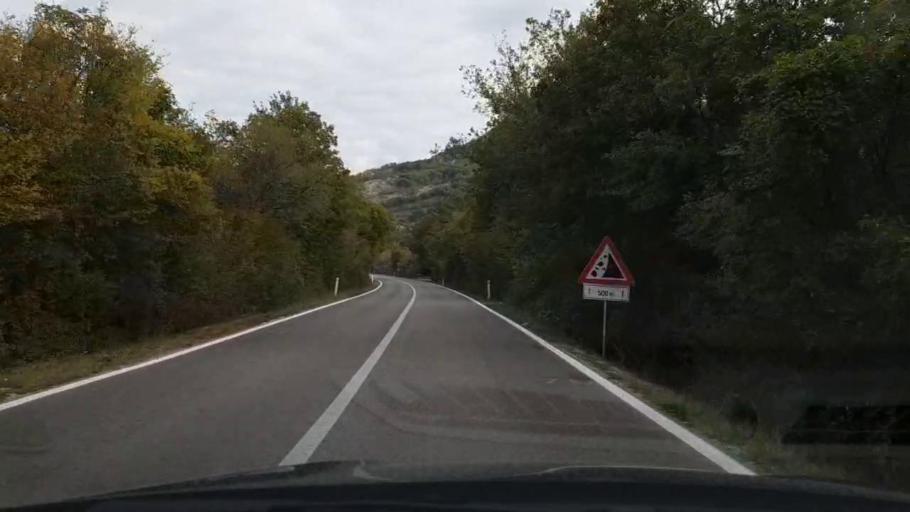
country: BA
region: Republika Srpska
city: Trebinje
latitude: 42.6880
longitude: 18.2623
